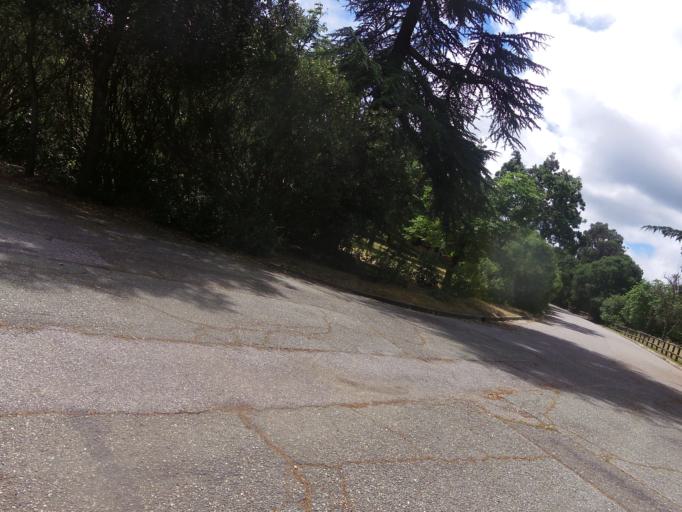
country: US
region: California
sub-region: Santa Clara County
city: Loyola
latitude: 37.3400
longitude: -122.0900
